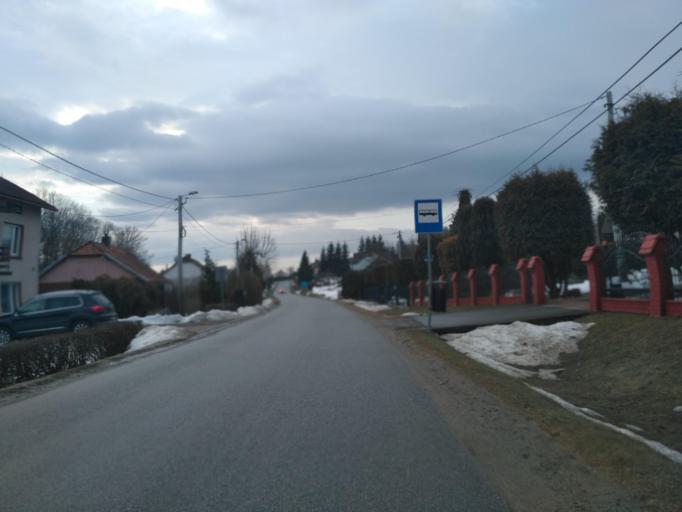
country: PL
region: Subcarpathian Voivodeship
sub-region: Powiat brzozowski
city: Dydnia
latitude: 49.6295
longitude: 22.1611
